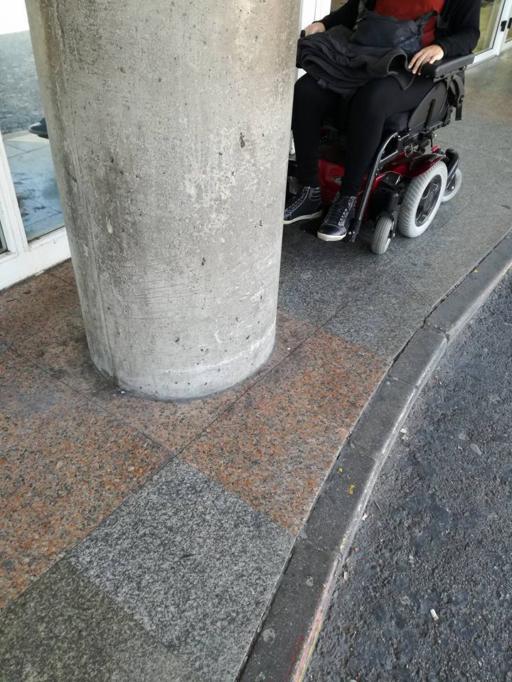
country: ES
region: Madrid
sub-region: Provincia de Madrid
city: Salamanca
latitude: 40.4191
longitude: -3.6697
